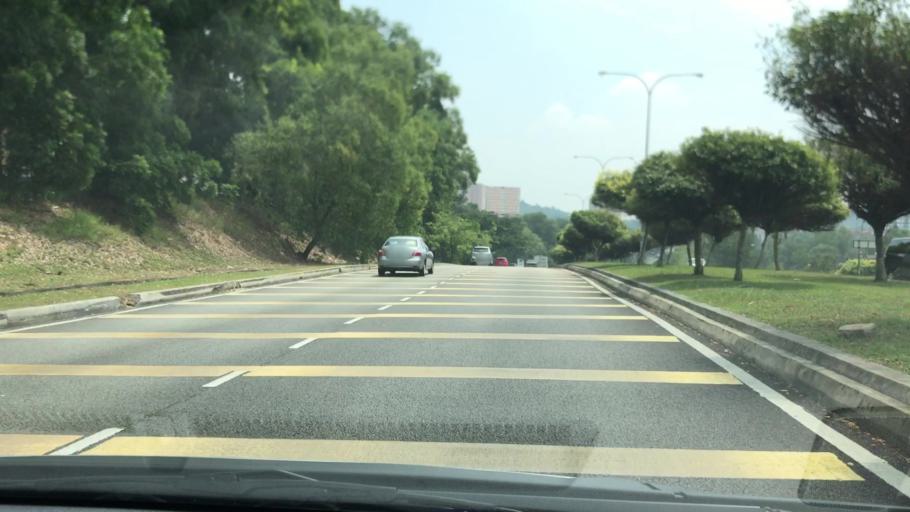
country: MY
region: Putrajaya
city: Putrajaya
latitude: 2.9996
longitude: 101.6649
